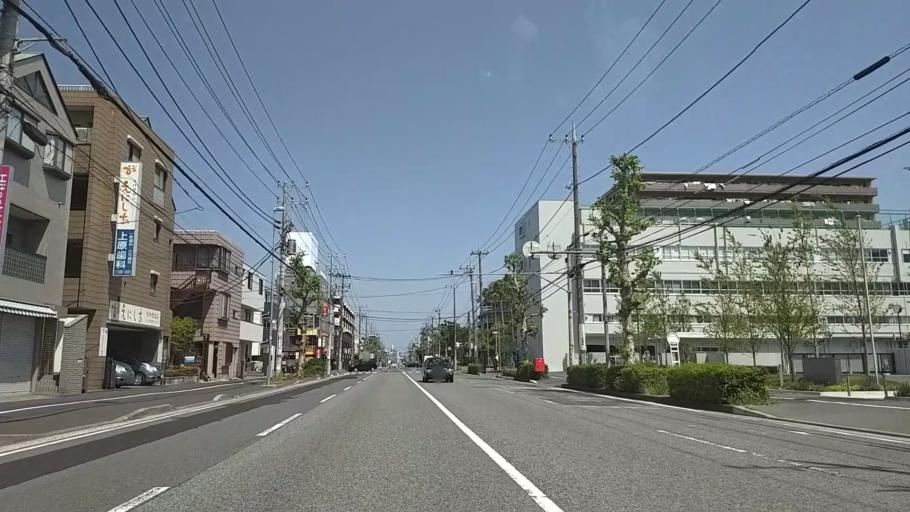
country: JP
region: Kanagawa
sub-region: Kawasaki-shi
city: Kawasaki
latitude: 35.5060
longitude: 139.6932
